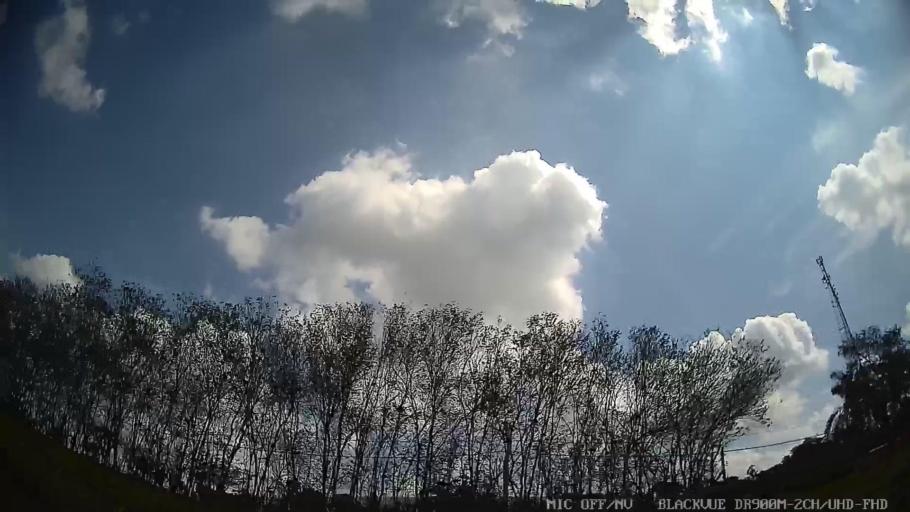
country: BR
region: Sao Paulo
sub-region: Itatiba
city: Itatiba
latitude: -22.9799
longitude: -46.7573
